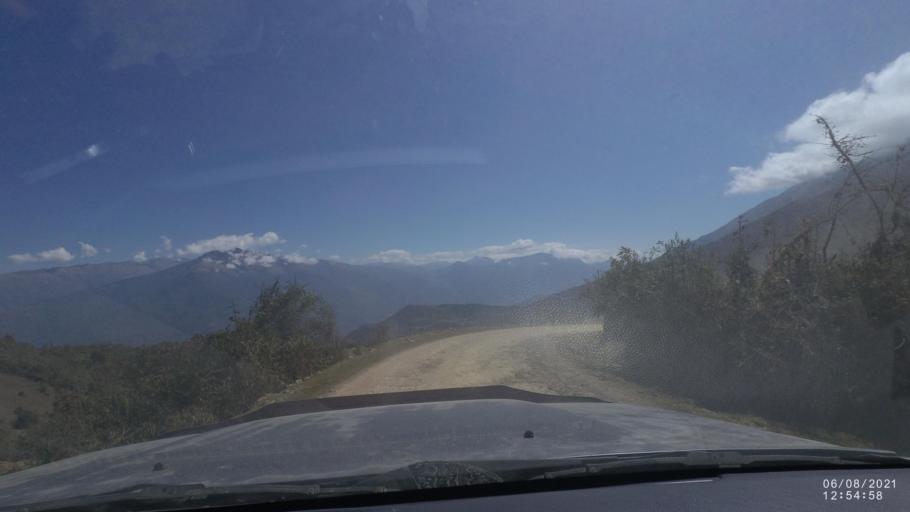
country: BO
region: Cochabamba
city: Colchani
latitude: -16.7563
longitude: -66.6817
